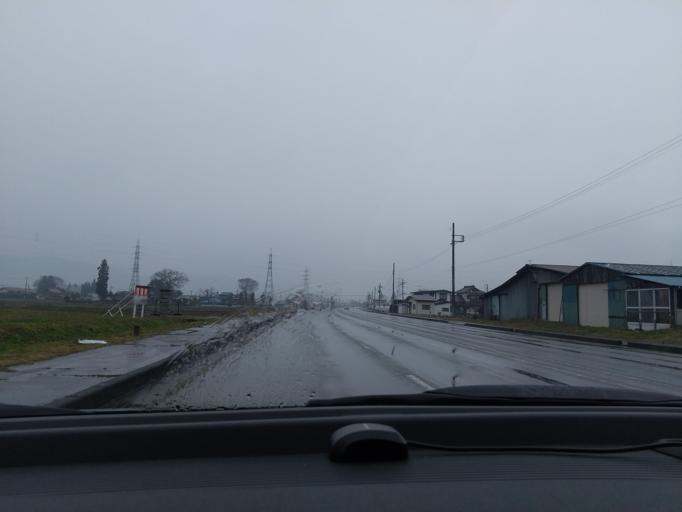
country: JP
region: Iwate
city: Morioka-shi
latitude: 39.6926
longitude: 141.0965
